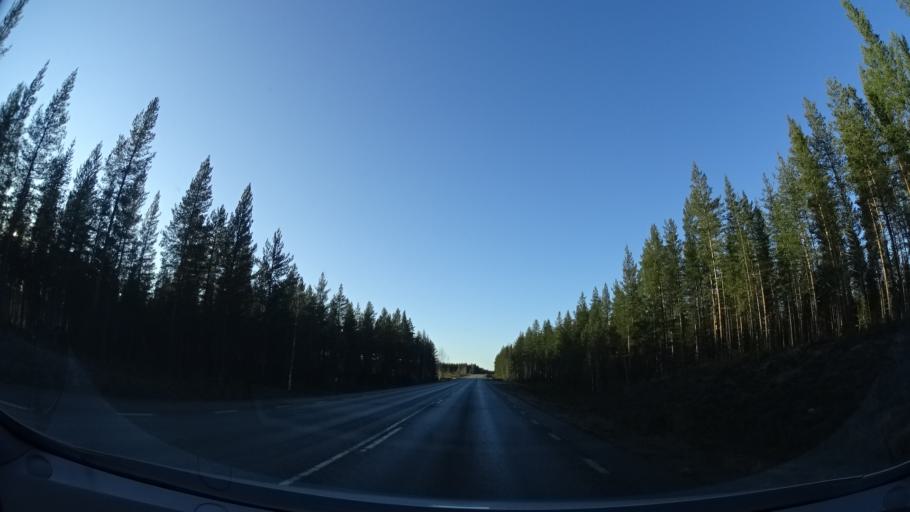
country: SE
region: Vaesterbotten
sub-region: Norsjo Kommun
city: Norsjoe
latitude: 64.9671
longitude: 19.7960
